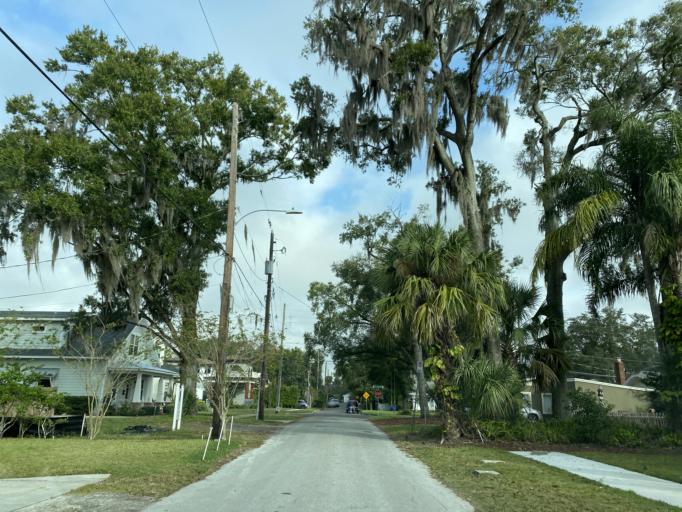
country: US
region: Florida
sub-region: Orange County
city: Orlando
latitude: 28.5619
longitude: -81.3883
